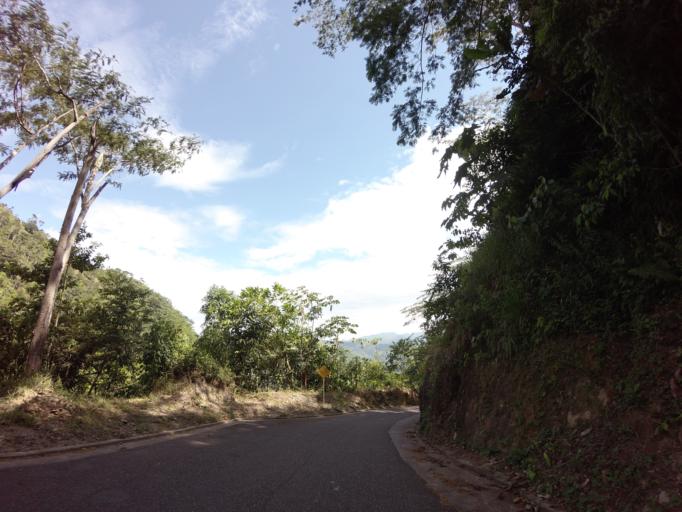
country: CO
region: Caldas
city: Norcasia
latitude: 5.5724
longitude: -74.8997
